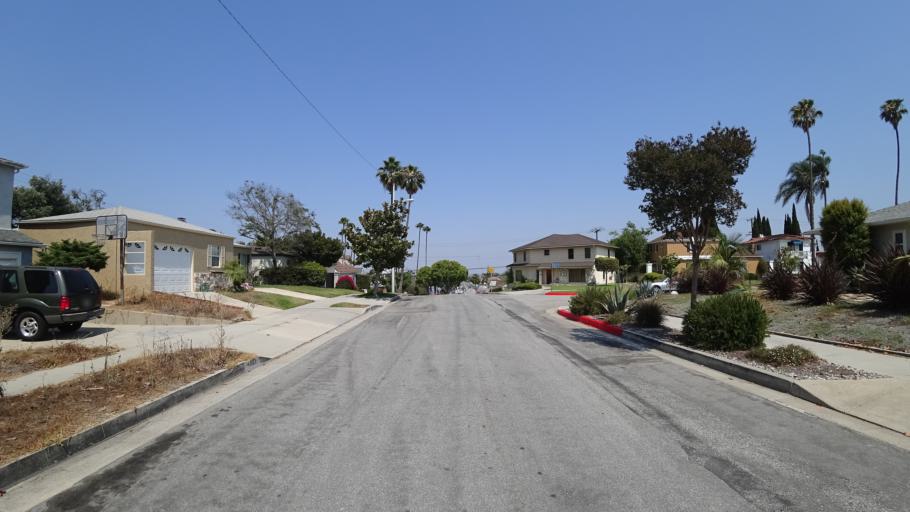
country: US
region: California
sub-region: Los Angeles County
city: View Park-Windsor Hills
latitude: 33.9880
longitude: -118.3556
